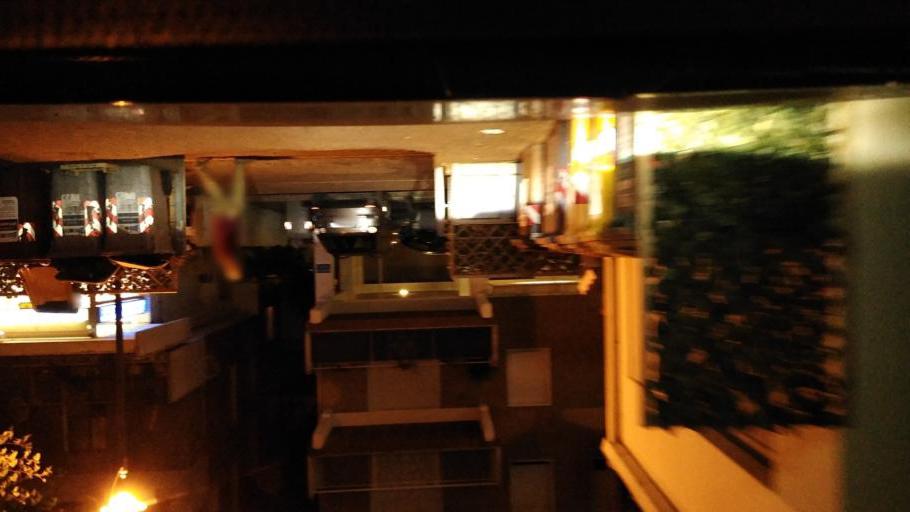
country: IT
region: Emilia-Romagna
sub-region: Provincia di Rimini
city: Bellaria-Igea Marina
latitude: 44.1332
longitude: 12.4829
